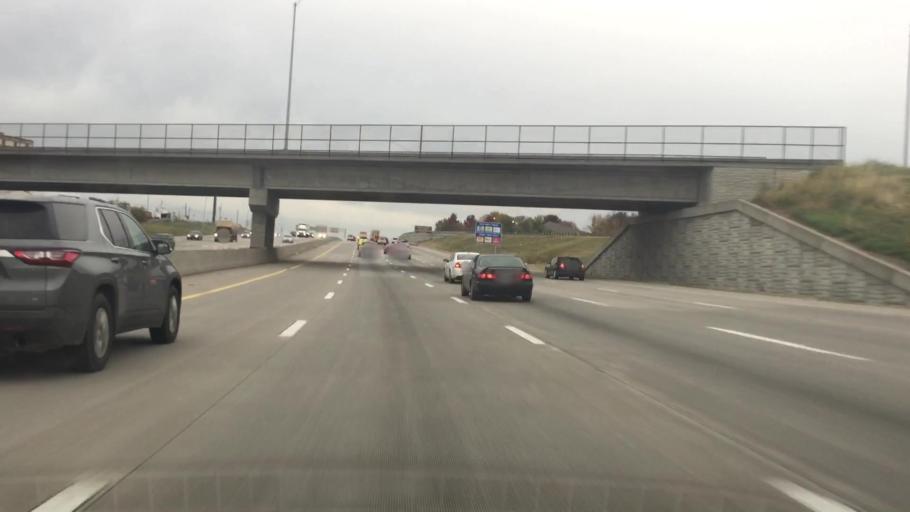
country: US
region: Missouri
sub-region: Jackson County
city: Grandview
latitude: 38.9169
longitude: -94.5272
